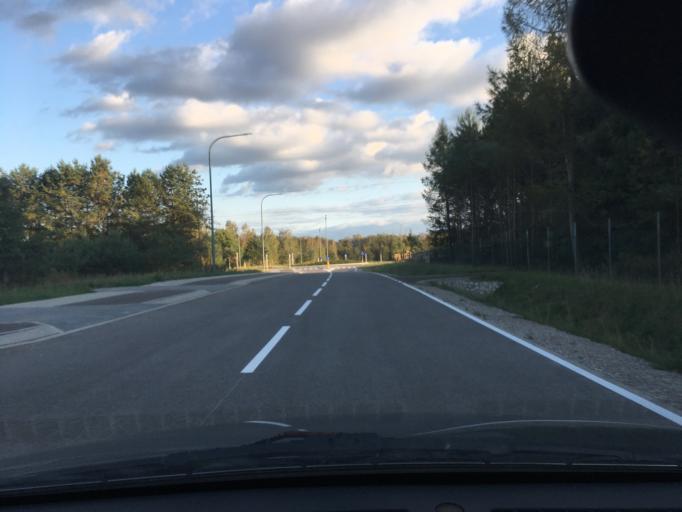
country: PL
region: Masovian Voivodeship
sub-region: Powiat piaseczynski
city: Lesznowola
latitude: 52.0462
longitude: 20.9260
